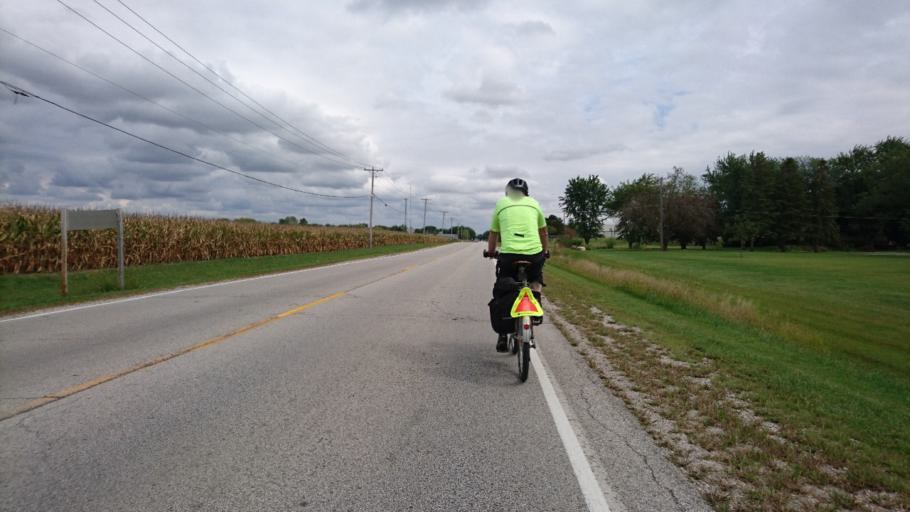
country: US
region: Illinois
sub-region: Livingston County
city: Pontiac
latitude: 40.8882
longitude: -88.6602
